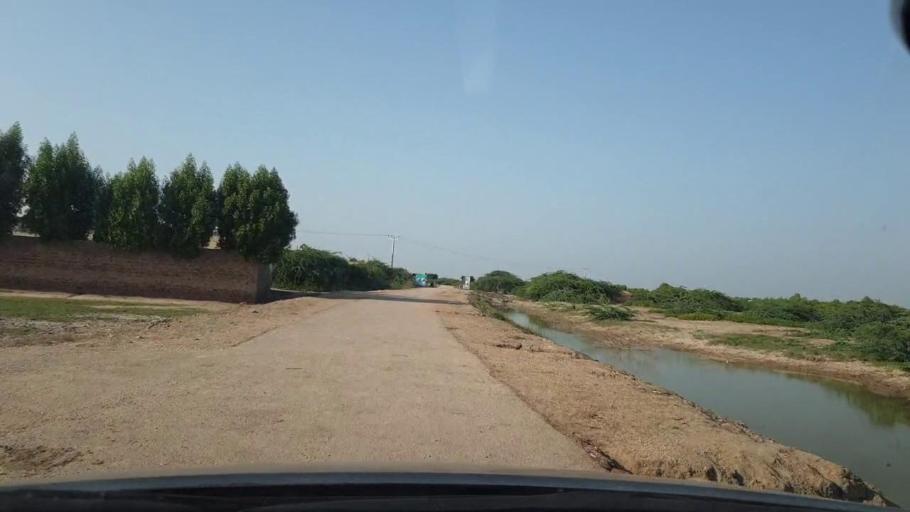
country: PK
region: Sindh
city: Naukot
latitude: 24.8365
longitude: 69.2224
